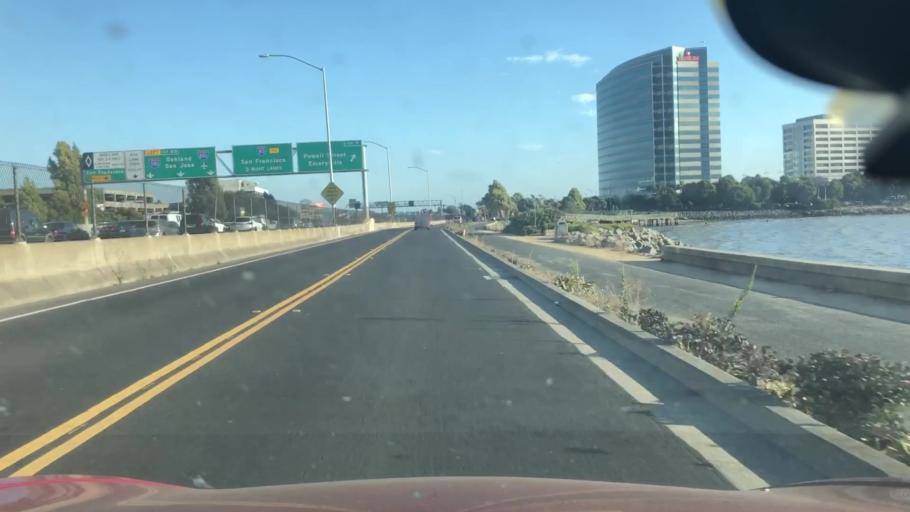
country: US
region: California
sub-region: Alameda County
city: Emeryville
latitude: 37.8432
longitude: -122.2980
